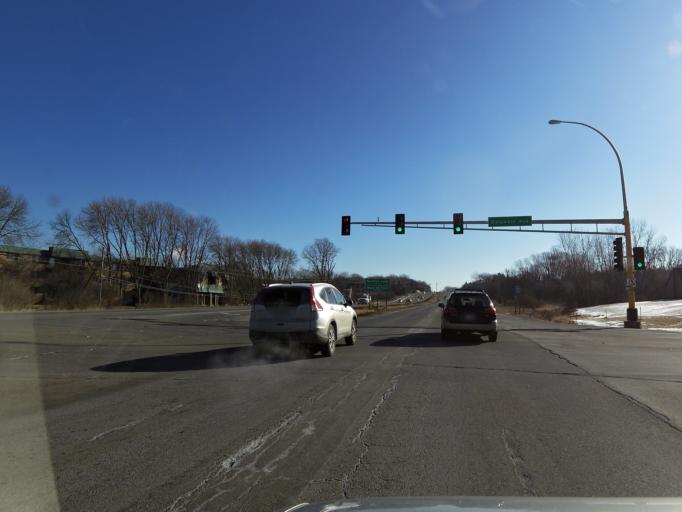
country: US
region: Minnesota
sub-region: Dakota County
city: Mendota Heights
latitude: 44.8834
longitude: -93.1062
